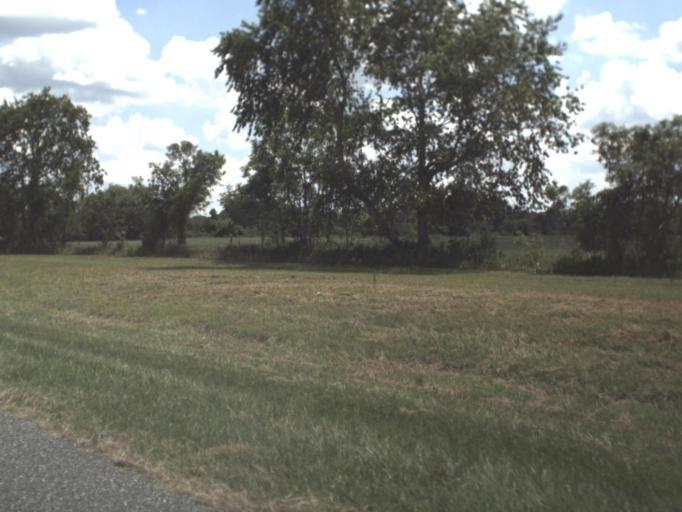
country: US
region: Florida
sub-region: Alachua County
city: High Springs
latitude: 29.9889
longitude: -82.5974
